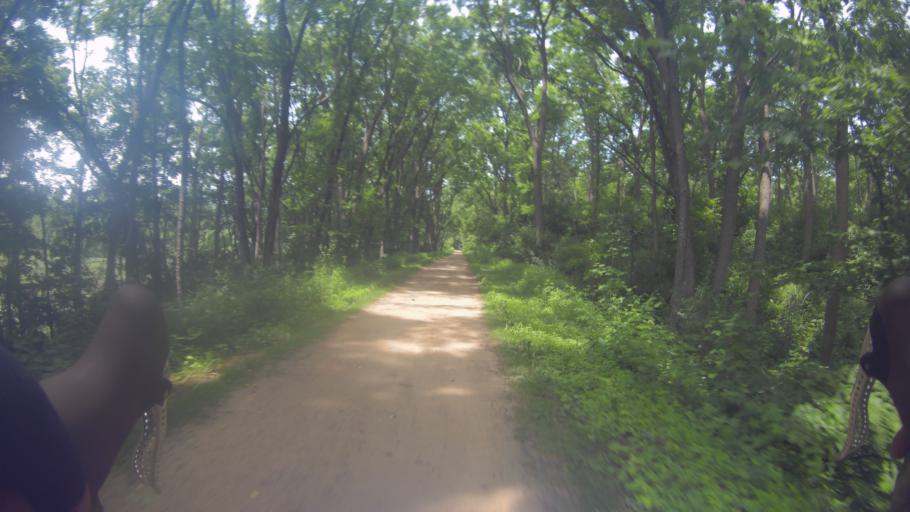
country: US
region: Wisconsin
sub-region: Dane County
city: Mount Horeb
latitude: 43.0151
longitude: -89.6964
